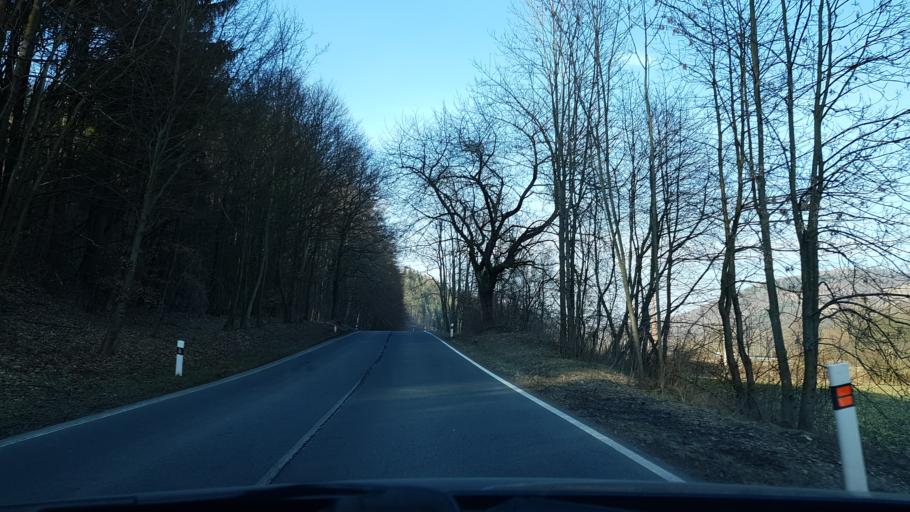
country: CZ
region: Olomoucky
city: Dolni Bohdikov
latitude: 50.0061
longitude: 16.8948
